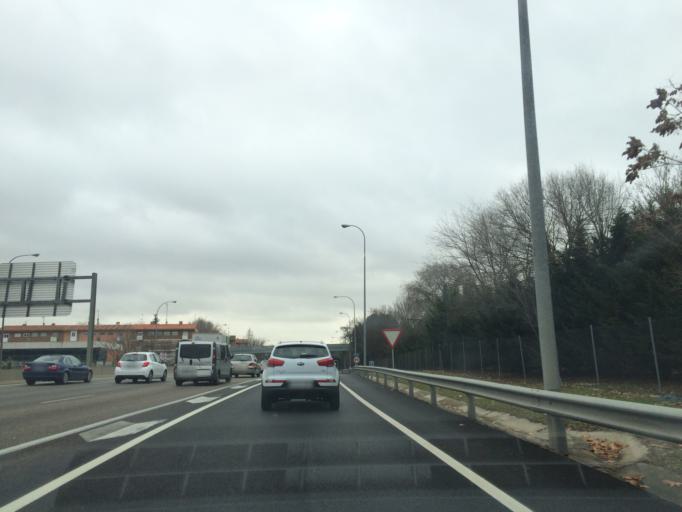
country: ES
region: Madrid
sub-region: Provincia de Madrid
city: Moncloa-Aravaca
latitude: 40.4333
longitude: -3.7381
